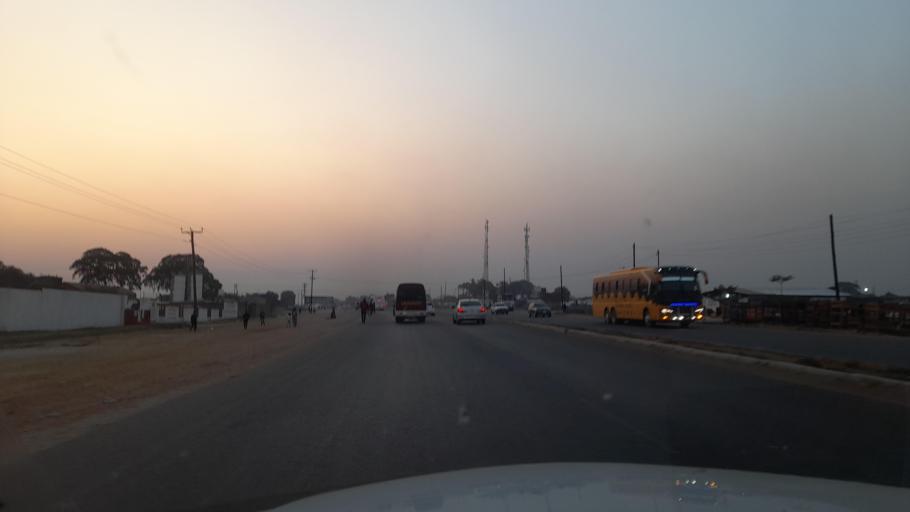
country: ZM
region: Copperbelt
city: Kitwe
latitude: -12.7762
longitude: 28.1921
